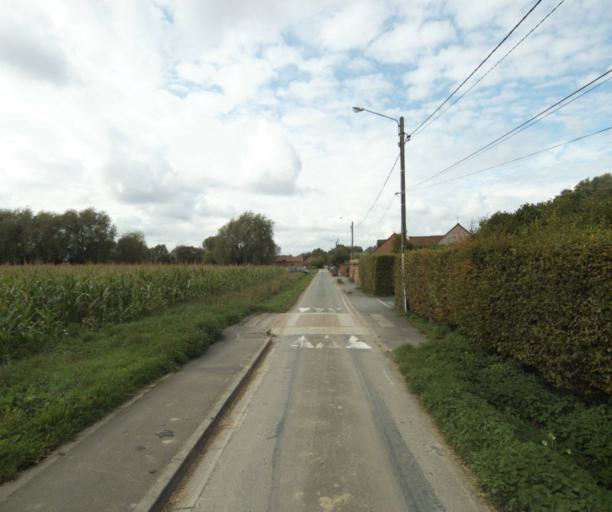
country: FR
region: Nord-Pas-de-Calais
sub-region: Departement du Nord
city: Premesques
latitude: 50.6638
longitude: 2.9521
